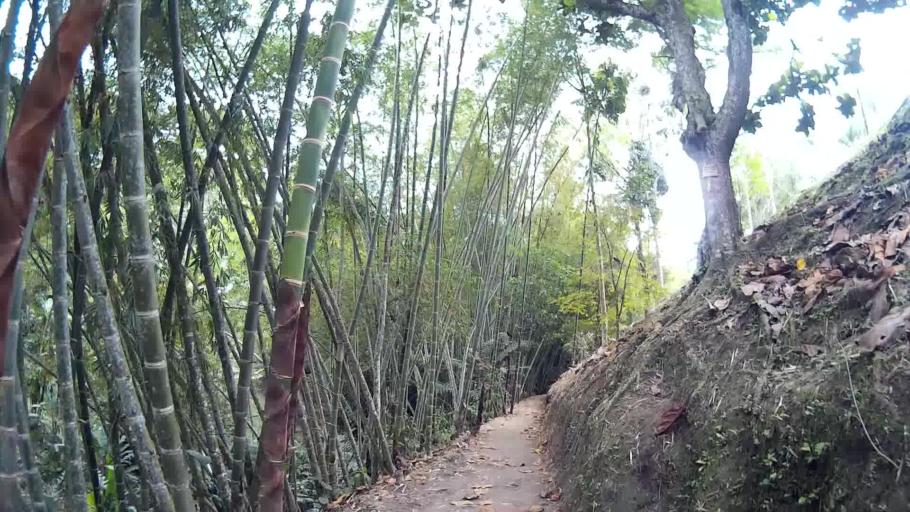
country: CO
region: Risaralda
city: Marsella
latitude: 4.9345
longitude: -75.7365
